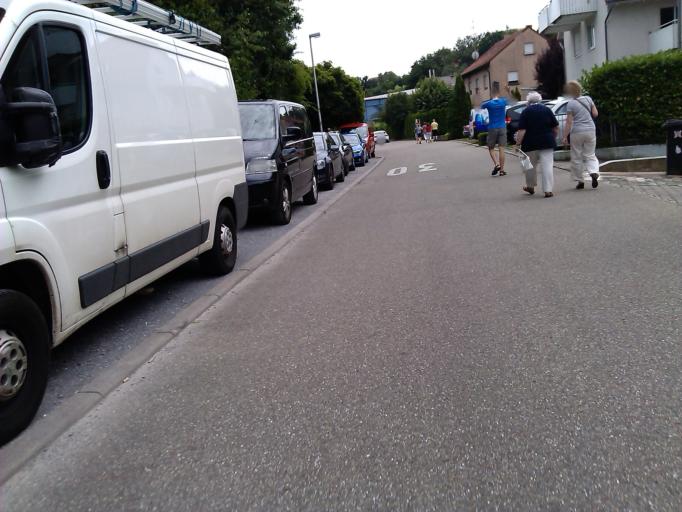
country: DE
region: Baden-Wuerttemberg
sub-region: Regierungsbezirk Stuttgart
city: Talheim
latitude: 49.0864
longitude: 9.1913
